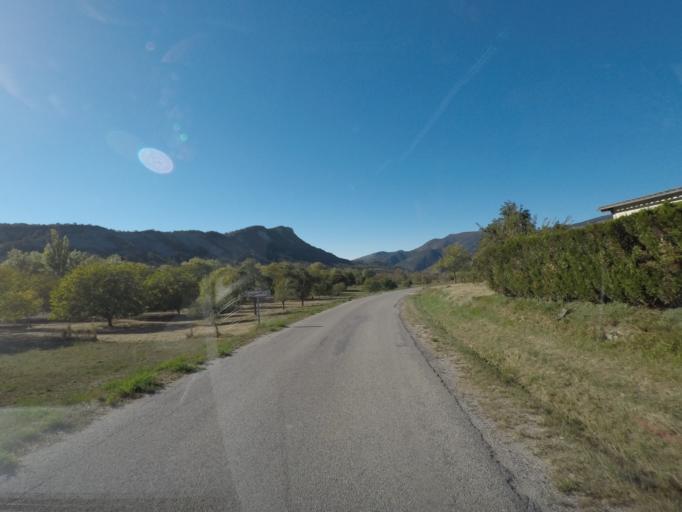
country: FR
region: Provence-Alpes-Cote d'Azur
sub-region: Departement des Hautes-Alpes
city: Serres
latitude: 44.4515
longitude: 5.5366
